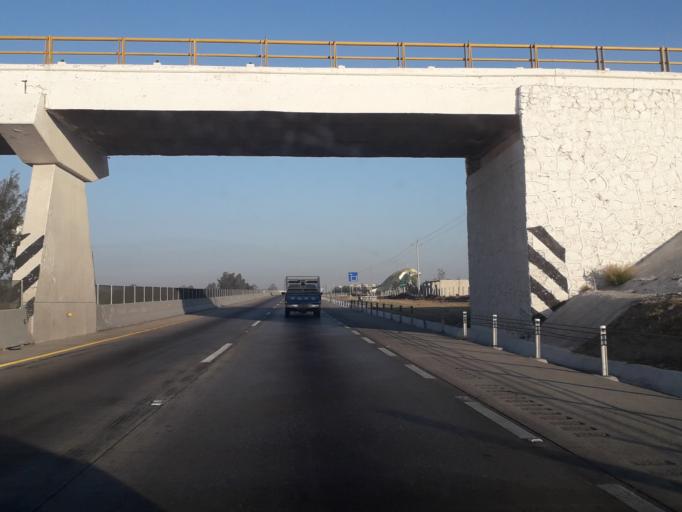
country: MX
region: Puebla
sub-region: Amozoc
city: Amozoc de Mota
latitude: 19.0465
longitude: -98.0205
